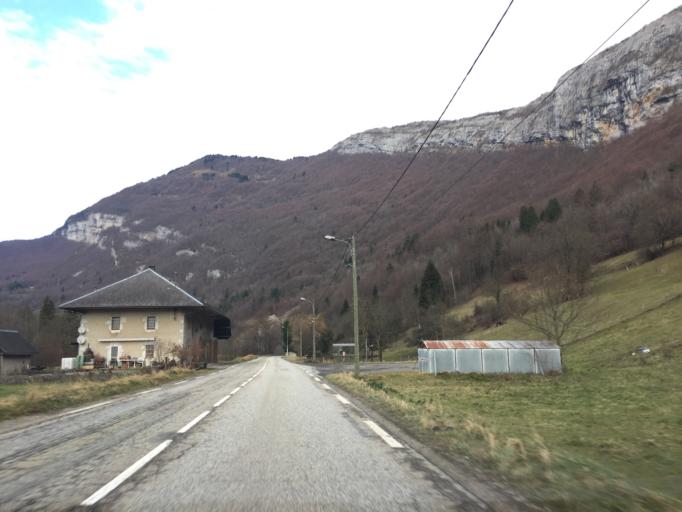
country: FR
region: Rhone-Alpes
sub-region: Departement de la Haute-Savoie
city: Gruffy
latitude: 45.7375
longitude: 6.0982
